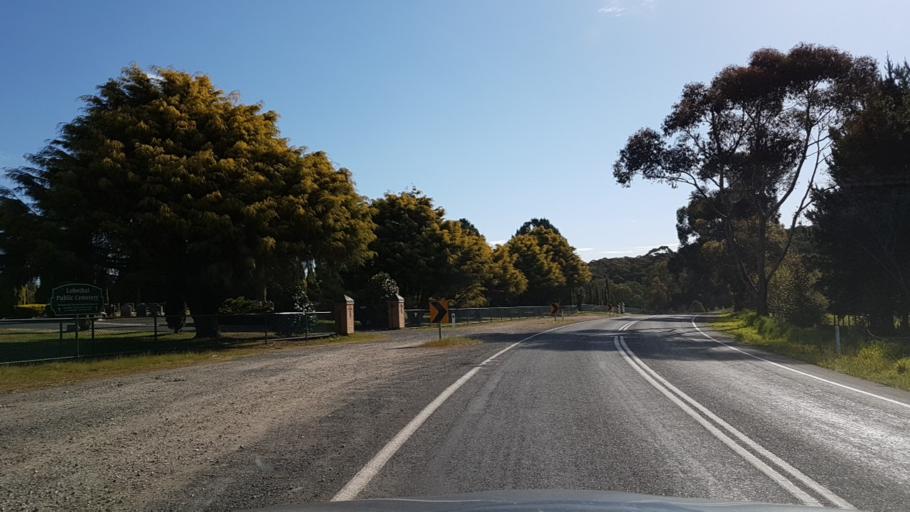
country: AU
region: South Australia
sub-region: Adelaide Hills
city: Lobethal
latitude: -34.8848
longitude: 138.8850
